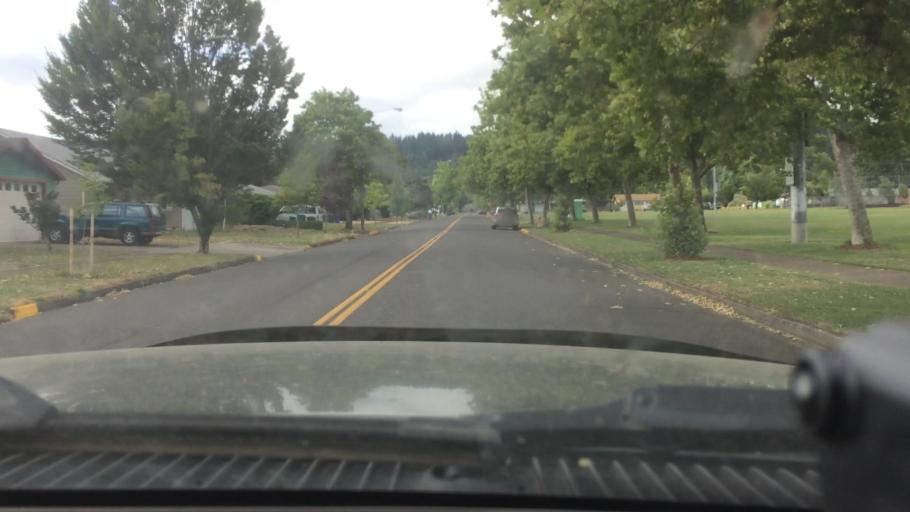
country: US
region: Oregon
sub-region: Lane County
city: Eugene
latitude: 44.0349
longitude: -123.1123
